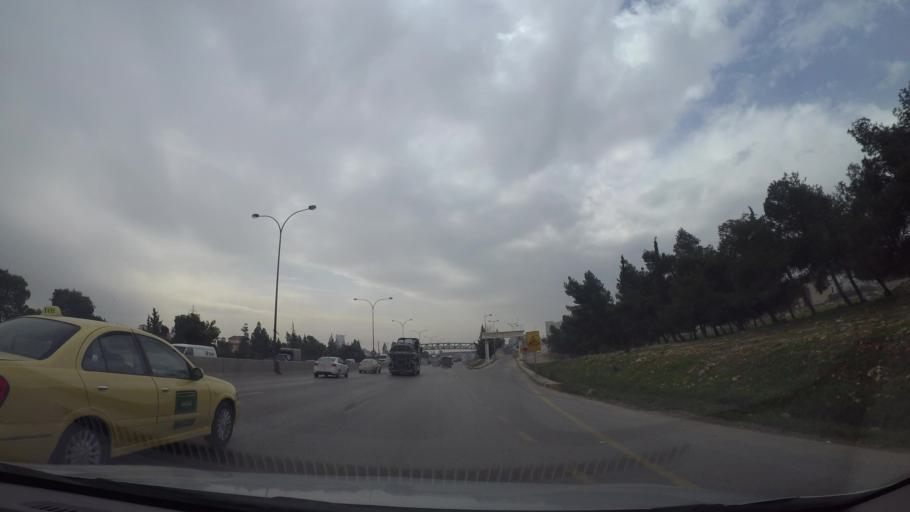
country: JO
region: Amman
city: Umm as Summaq
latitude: 31.9257
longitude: 35.8599
